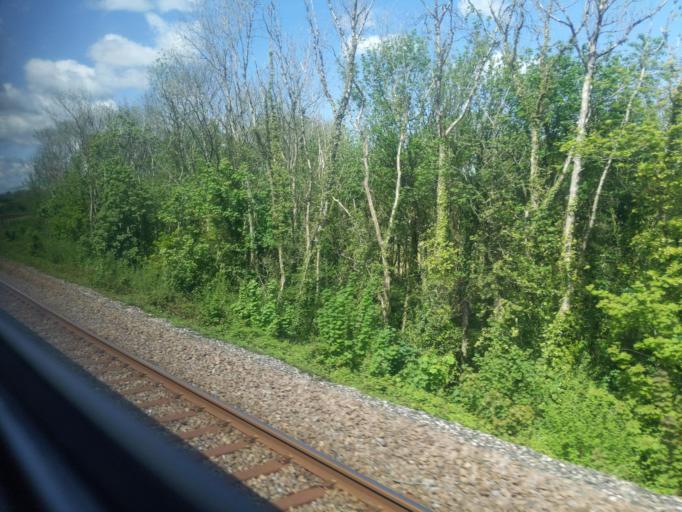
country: GB
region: England
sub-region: Cornwall
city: Pillaton
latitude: 50.4121
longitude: -4.3542
